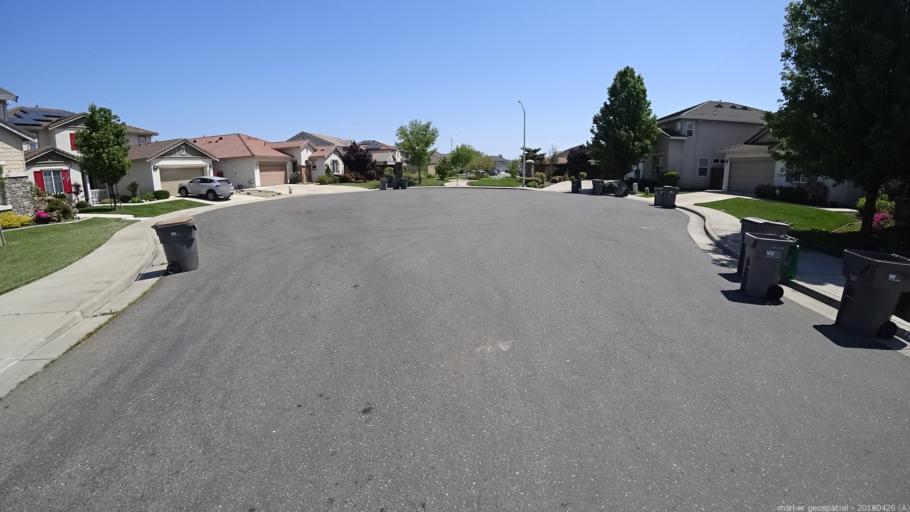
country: US
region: California
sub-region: Yolo County
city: West Sacramento
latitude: 38.5255
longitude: -121.5787
